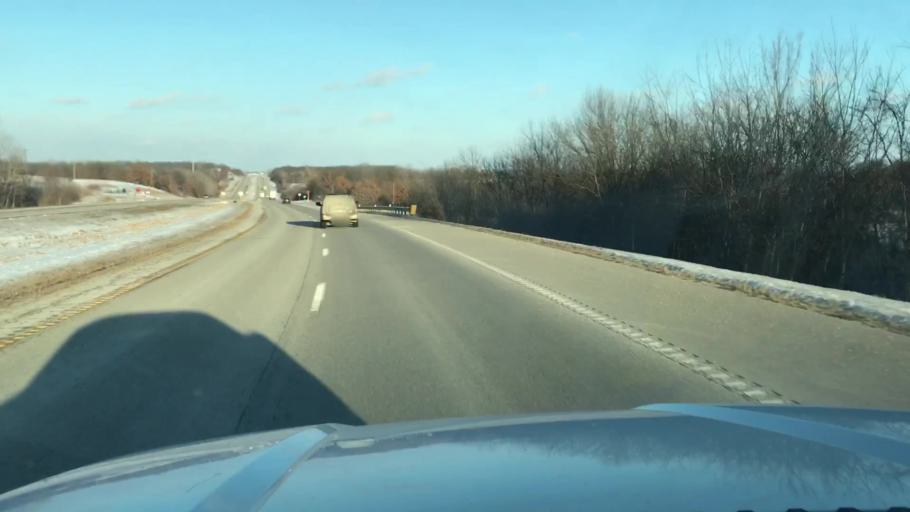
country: US
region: Missouri
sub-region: Clinton County
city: Gower
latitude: 39.7474
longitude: -94.6050
